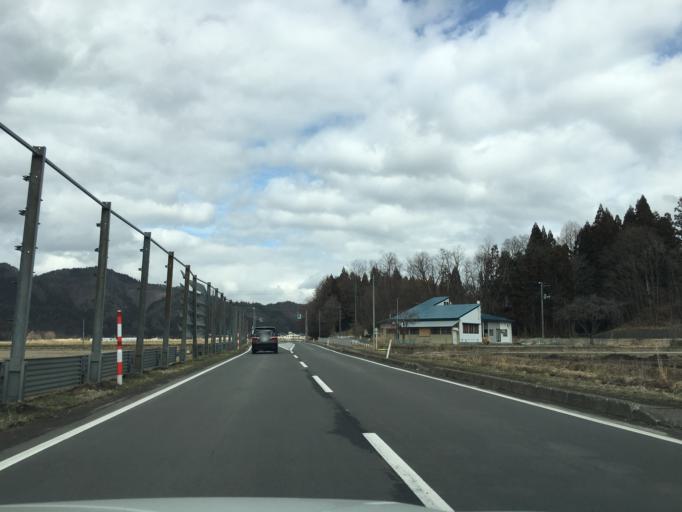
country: JP
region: Akita
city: Hanawa
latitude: 40.2350
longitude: 140.7353
